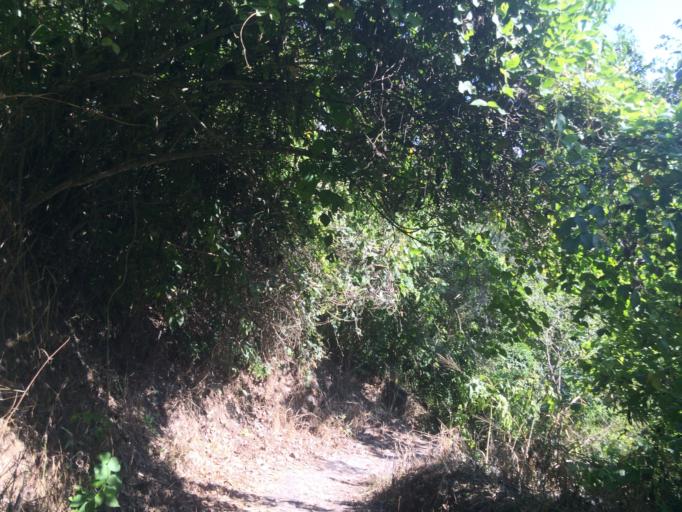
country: MX
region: Colima
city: Suchitlan
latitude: 19.3741
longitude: -103.7070
